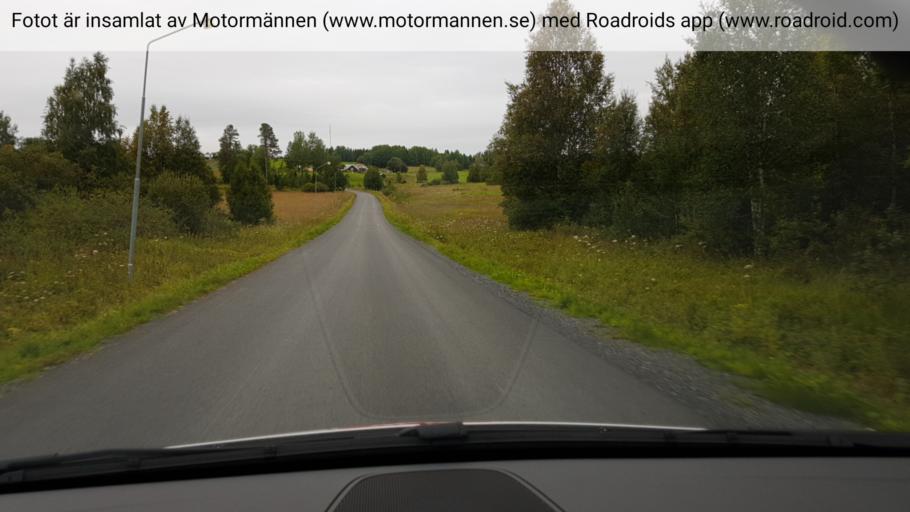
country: SE
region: Jaemtland
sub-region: OEstersunds Kommun
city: Lit
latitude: 63.5614
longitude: 14.9508
